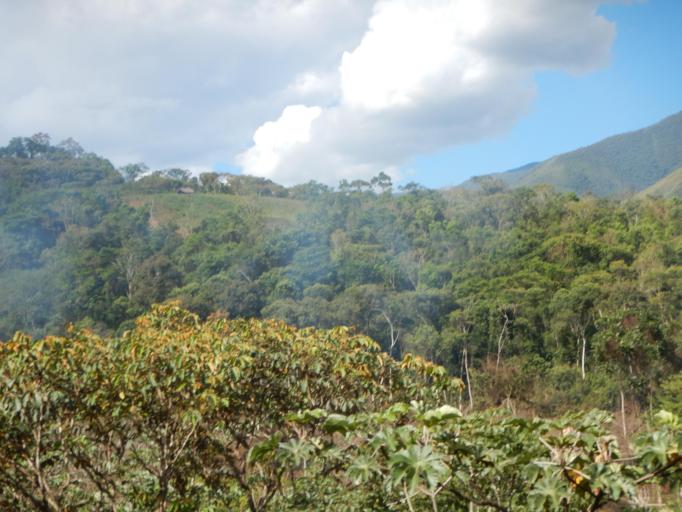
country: BO
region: La Paz
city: Coroico
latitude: -16.1637
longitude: -67.7290
